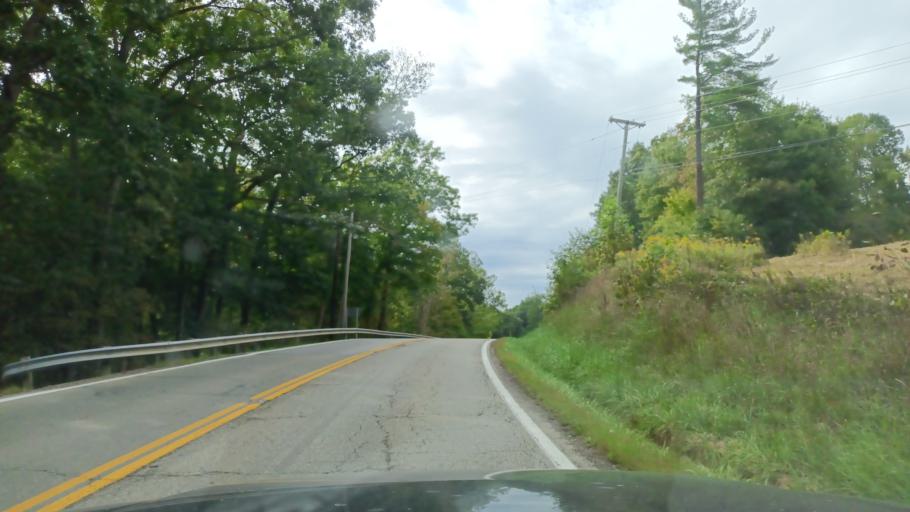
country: US
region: Ohio
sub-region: Vinton County
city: McArthur
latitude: 39.2715
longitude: -82.5619
